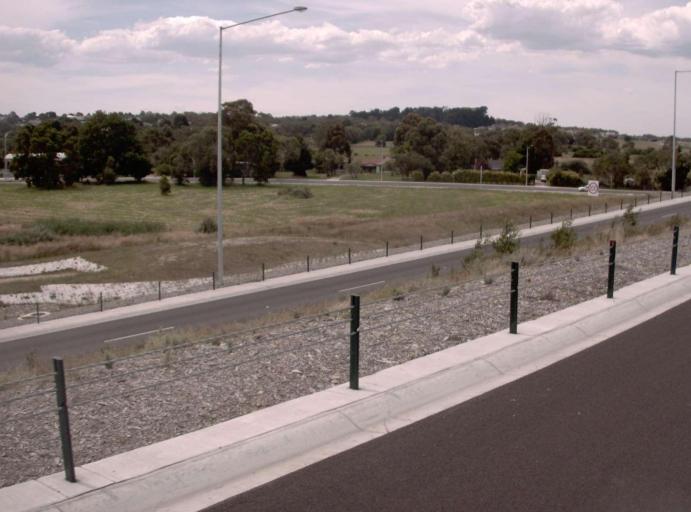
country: AU
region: Victoria
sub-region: Mornington Peninsula
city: Baxter
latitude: -38.1960
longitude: 145.1507
